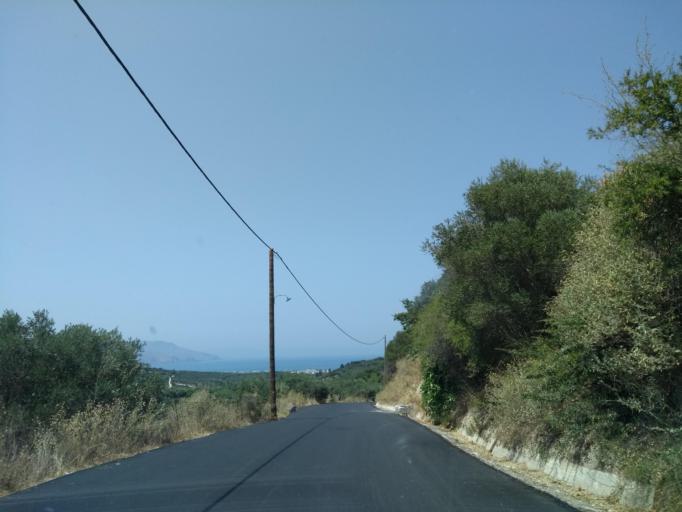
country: GR
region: Crete
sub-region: Nomos Chanias
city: Georgioupolis
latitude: 35.3230
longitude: 24.2999
